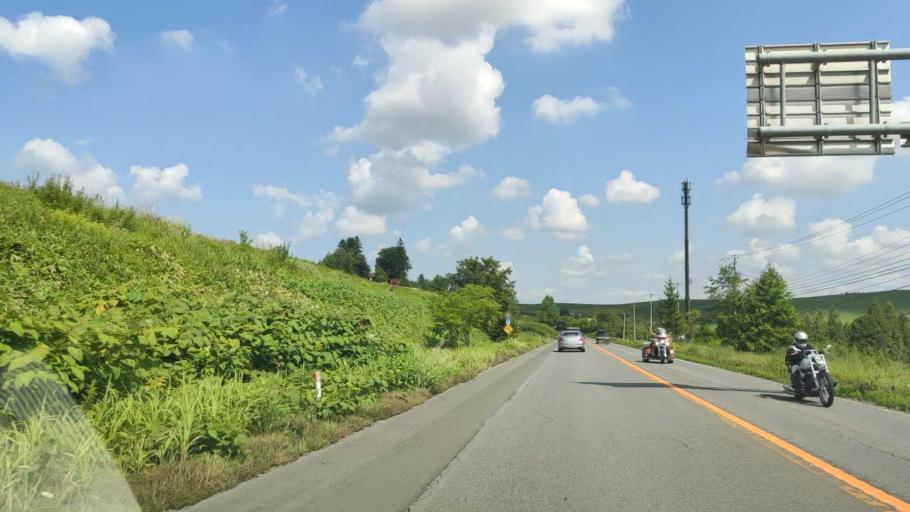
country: JP
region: Hokkaido
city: Shimo-furano
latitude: 43.5485
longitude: 142.4392
